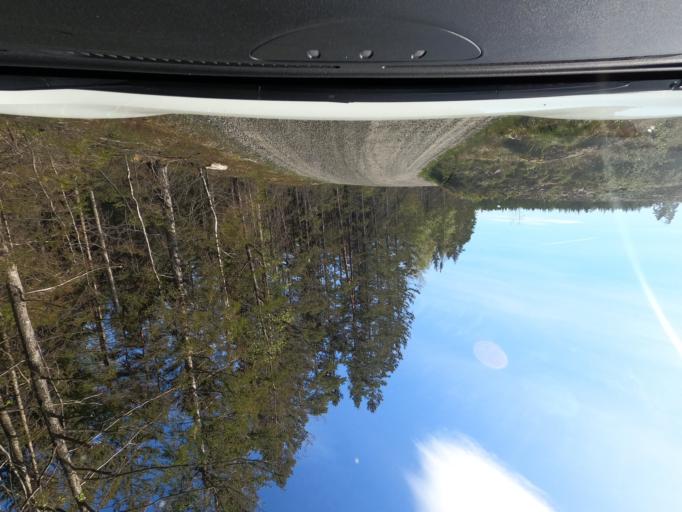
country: SE
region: Vaestra Goetaland
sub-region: Harryda Kommun
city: Ravlanda
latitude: 57.5960
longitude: 12.4765
